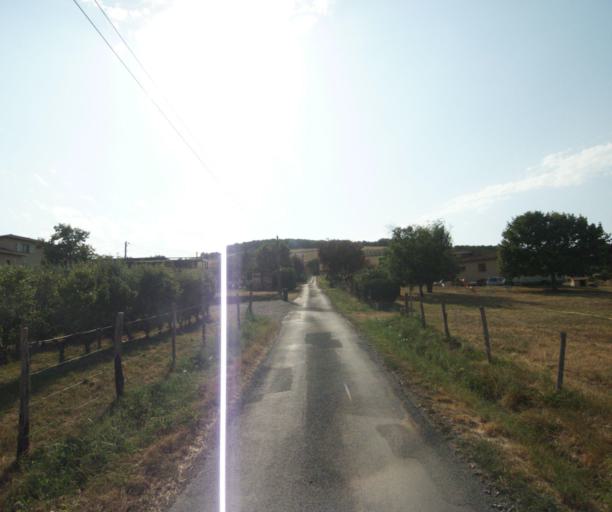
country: FR
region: Rhone-Alpes
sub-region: Departement du Rhone
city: Savigny
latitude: 45.8304
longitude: 4.5741
